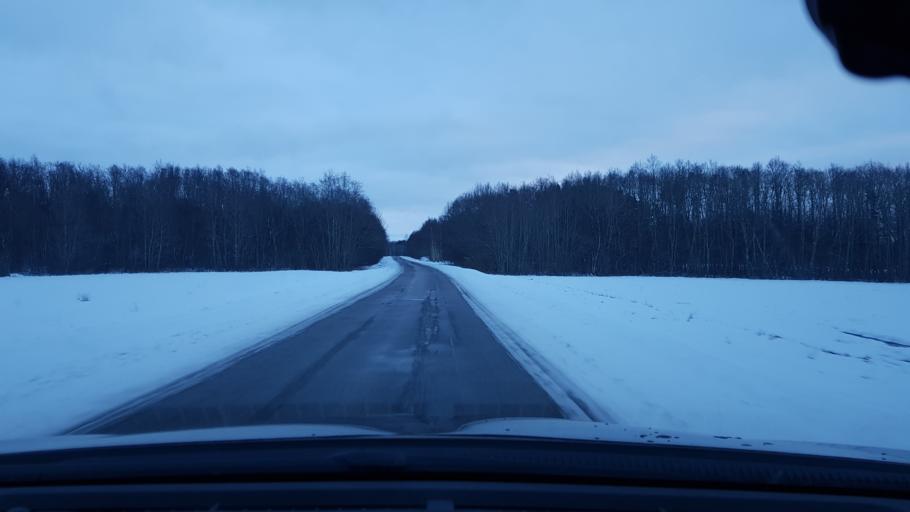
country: EE
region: Laeaene
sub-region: Haapsalu linn
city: Haapsalu
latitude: 59.0794
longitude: 23.5605
